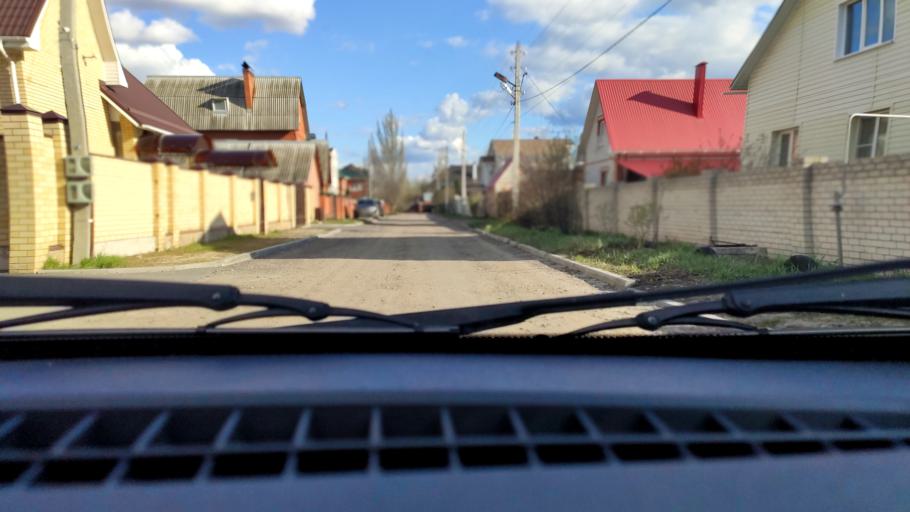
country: RU
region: Voronezj
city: Somovo
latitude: 51.6801
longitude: 39.3194
